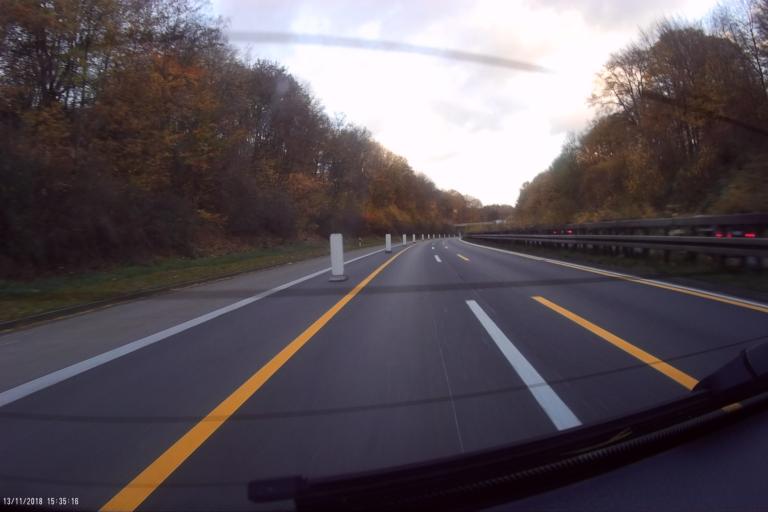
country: DE
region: North Rhine-Westphalia
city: Sprockhovel
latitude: 51.3306
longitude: 7.2668
